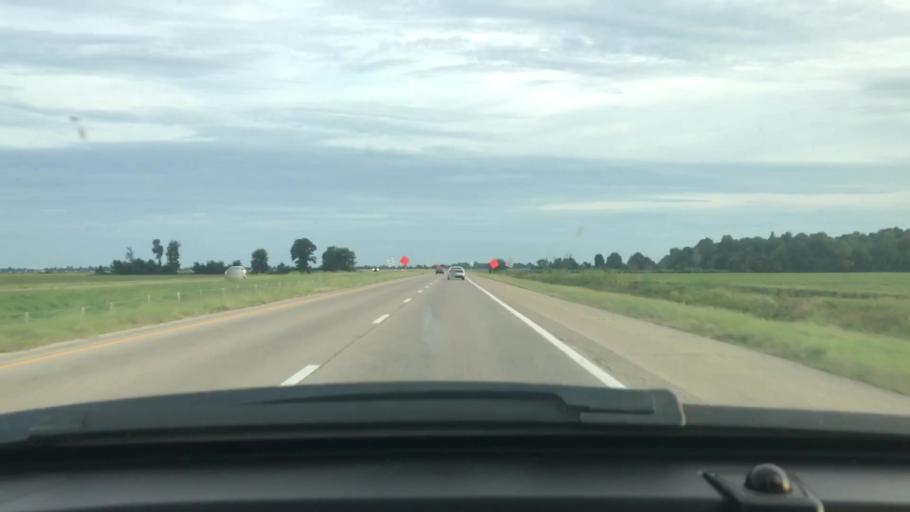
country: US
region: Arkansas
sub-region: Craighead County
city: Bay
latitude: 35.7237
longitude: -90.5802
